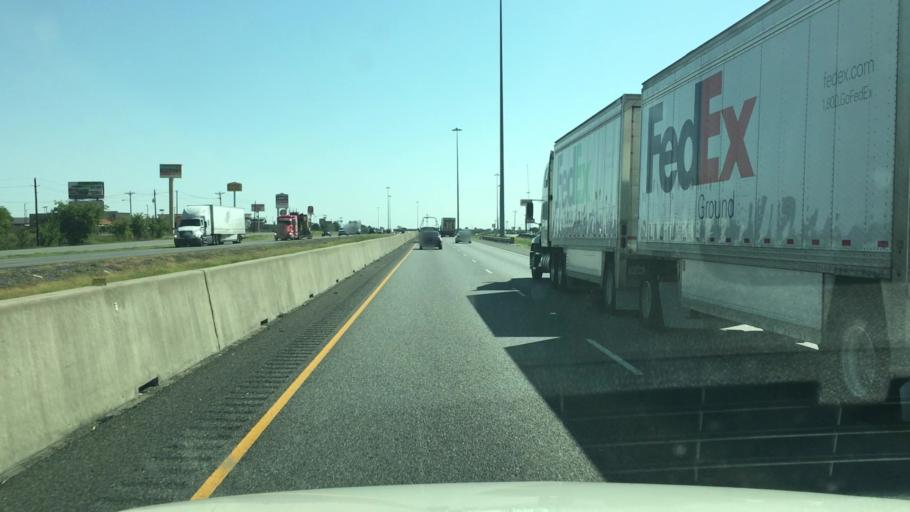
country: US
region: Texas
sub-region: Hunt County
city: Greenville
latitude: 33.0921
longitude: -96.1181
